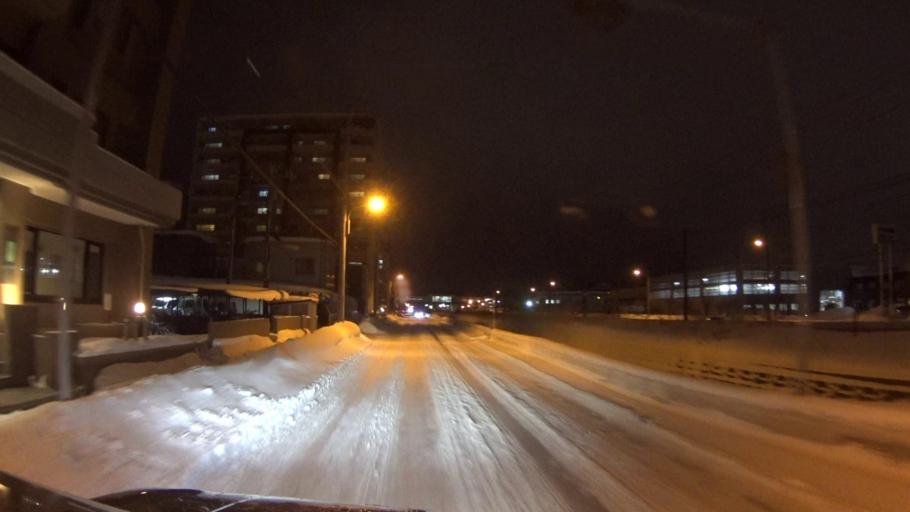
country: JP
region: Hokkaido
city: Sapporo
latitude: 43.0975
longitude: 141.2807
